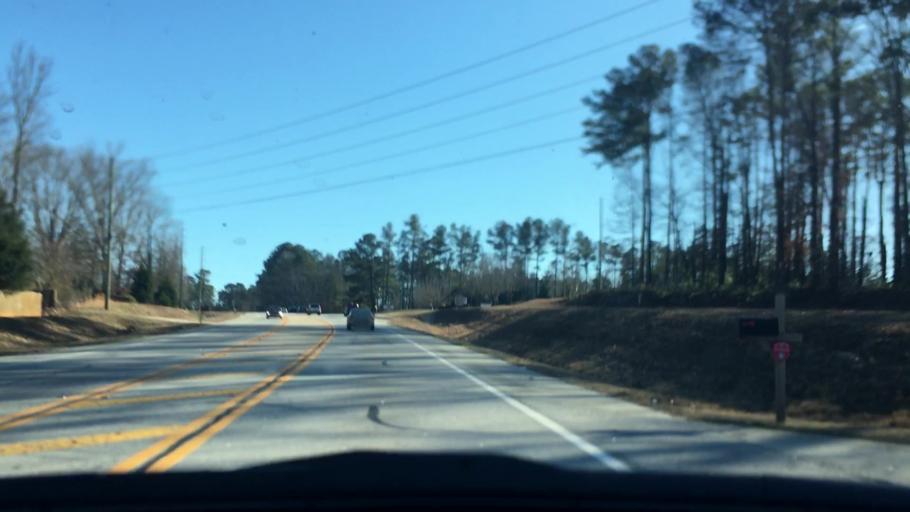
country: US
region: Georgia
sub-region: Henry County
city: McDonough
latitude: 33.5236
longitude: -84.1398
